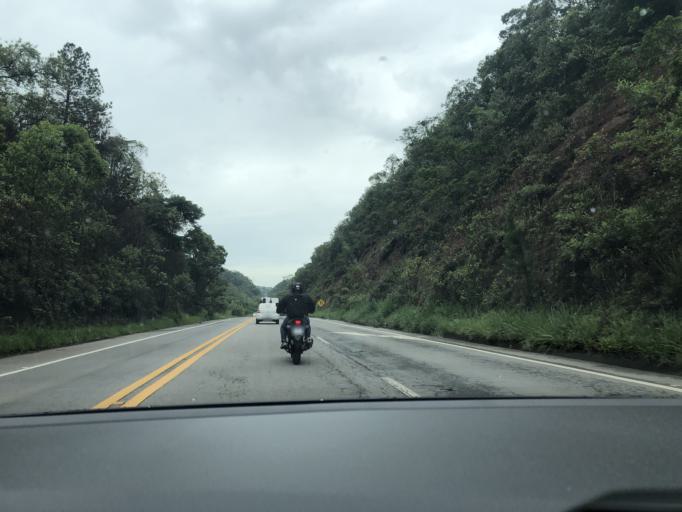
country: BR
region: Sao Paulo
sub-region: Jarinu
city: Jarinu
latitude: -23.1542
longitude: -46.7460
